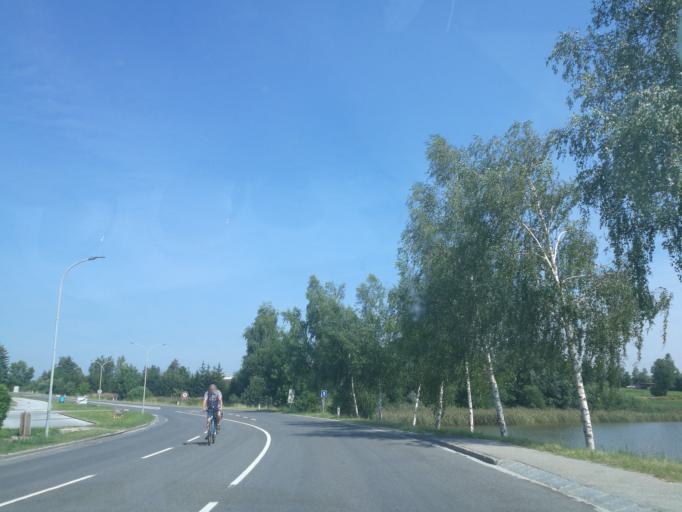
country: AT
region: Lower Austria
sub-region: Politischer Bezirk Gmund
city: Heidenreichstein
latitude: 48.8703
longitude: 15.1220
